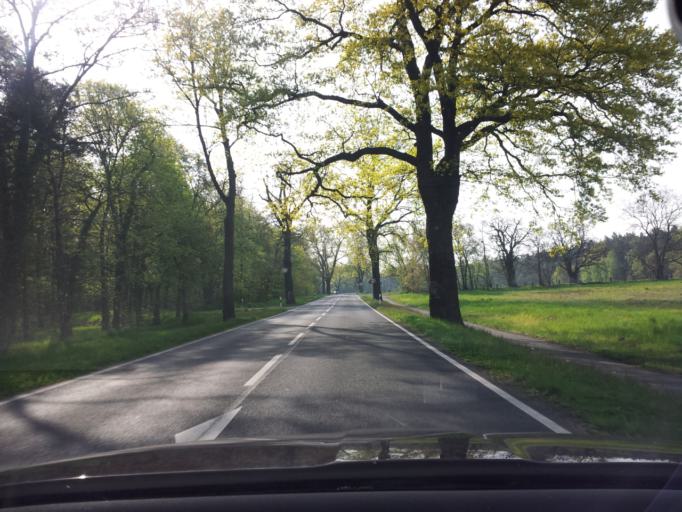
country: DE
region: Brandenburg
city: Juterbog
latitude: 51.9972
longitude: 13.0356
